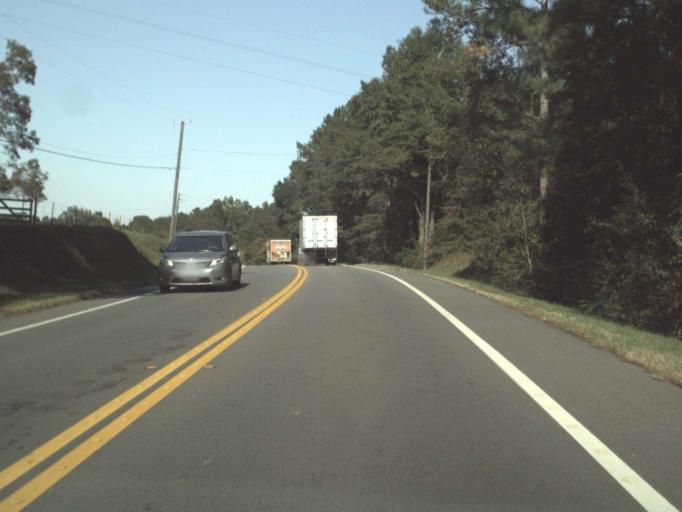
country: US
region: Alabama
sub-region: Covington County
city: Florala
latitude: 30.9843
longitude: -86.3412
